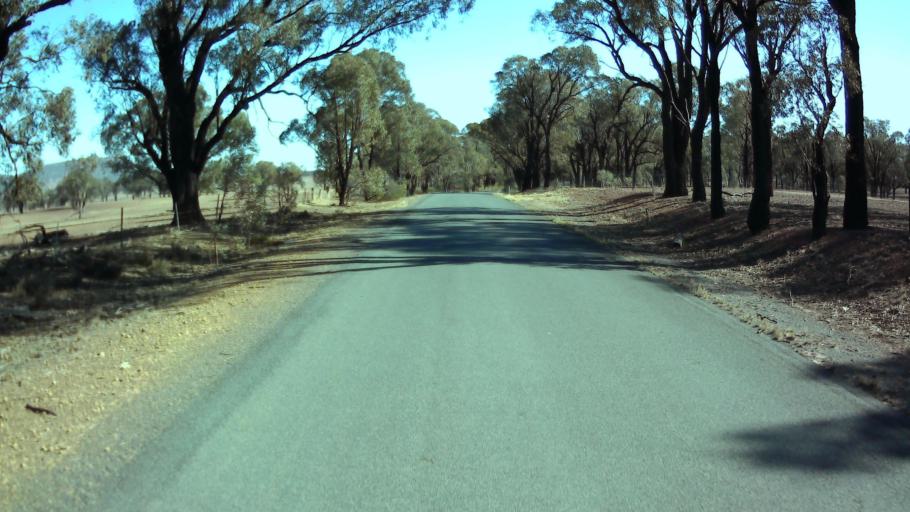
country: AU
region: New South Wales
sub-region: Weddin
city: Grenfell
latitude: -33.7866
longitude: 147.9582
